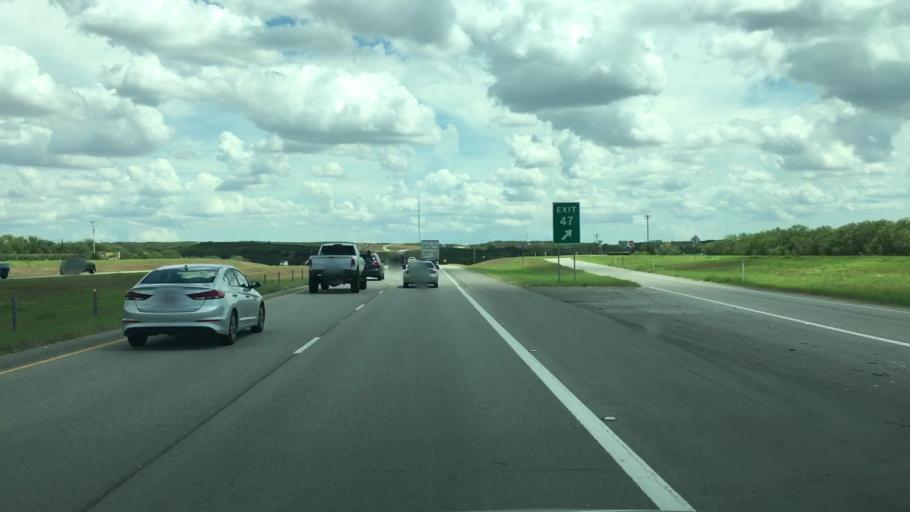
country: US
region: Texas
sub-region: Live Oak County
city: George West
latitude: 28.2655
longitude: -97.9371
